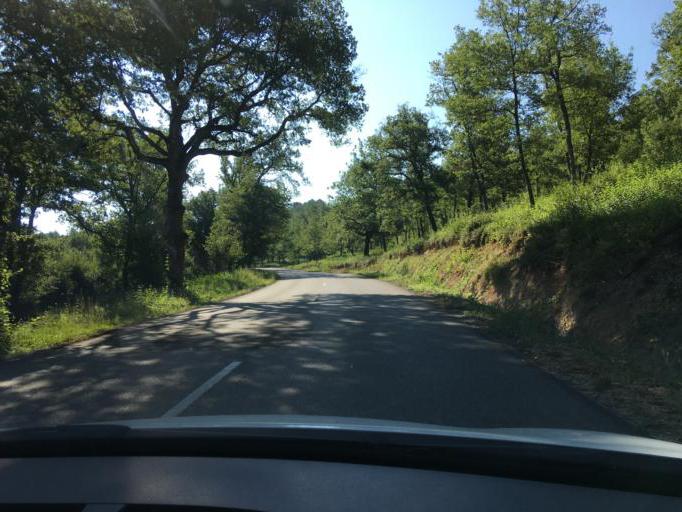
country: FR
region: Provence-Alpes-Cote d'Azur
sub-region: Departement des Alpes-de-Haute-Provence
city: Greoux-les-Bains
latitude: 43.7919
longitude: 5.8418
